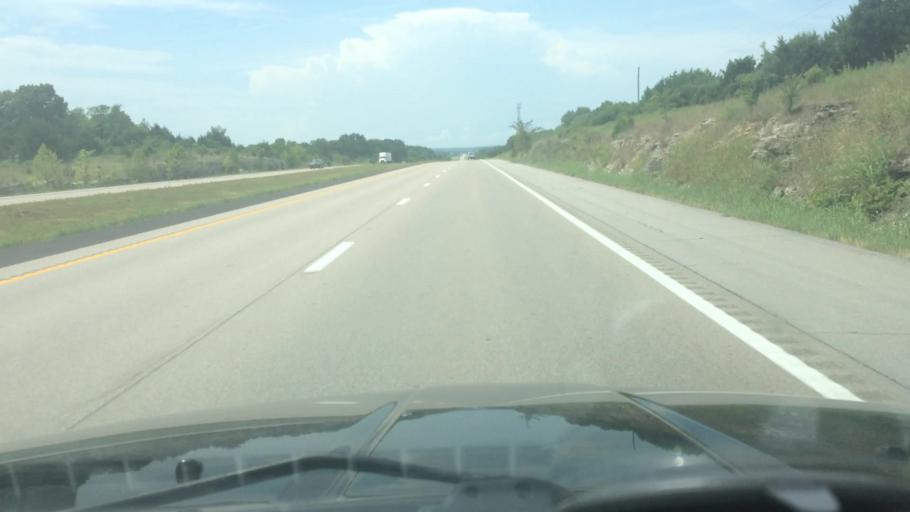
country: US
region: Missouri
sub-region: Polk County
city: Humansville
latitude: 37.7738
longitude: -93.5688
